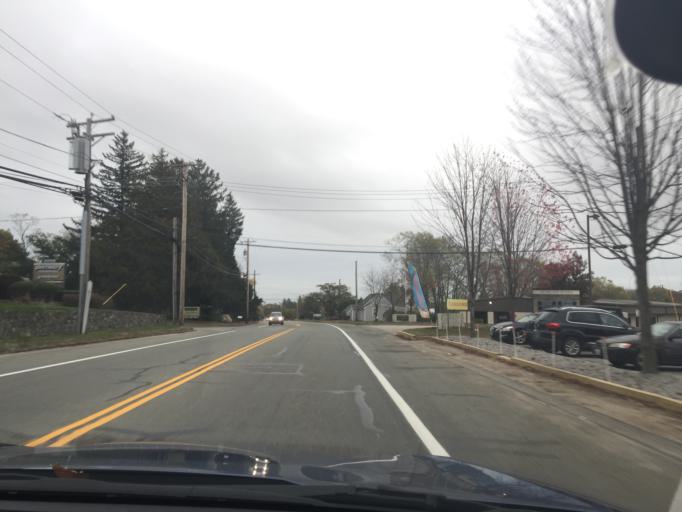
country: US
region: Rhode Island
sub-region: Providence County
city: Johnston
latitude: 41.7906
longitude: -71.5275
